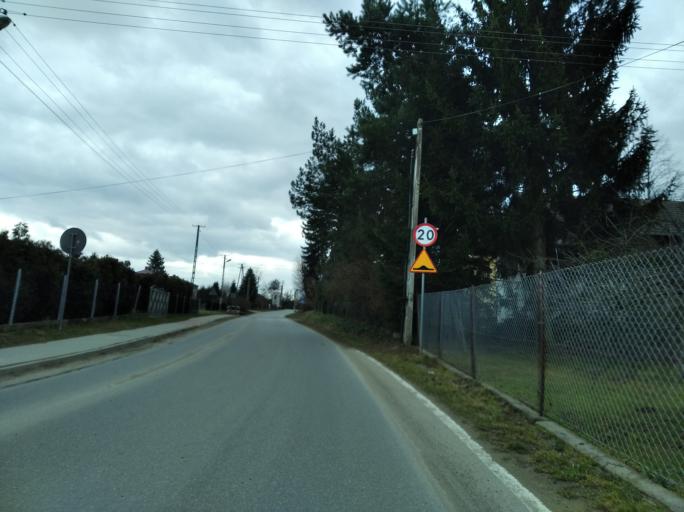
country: PL
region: Subcarpathian Voivodeship
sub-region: Powiat krosnienski
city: Odrzykon
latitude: 49.7585
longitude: 21.7148
